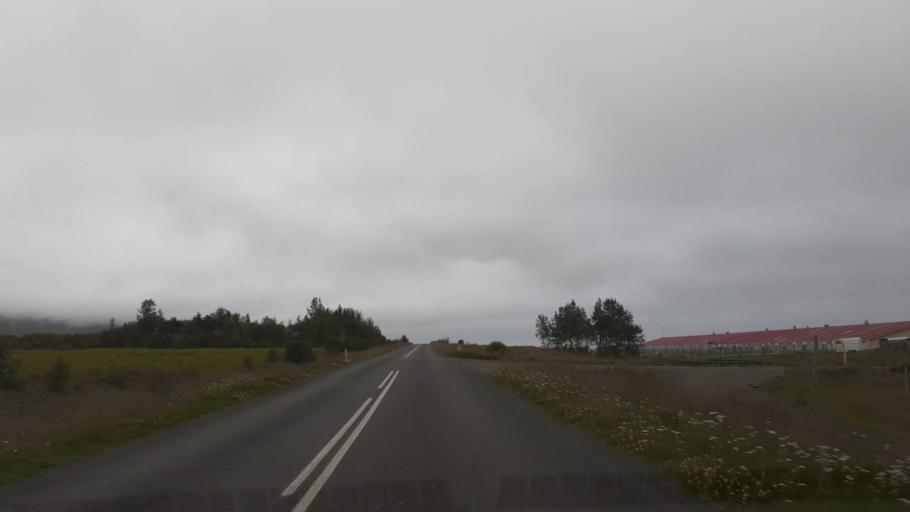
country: IS
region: Northeast
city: Dalvik
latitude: 65.9485
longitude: -18.5559
